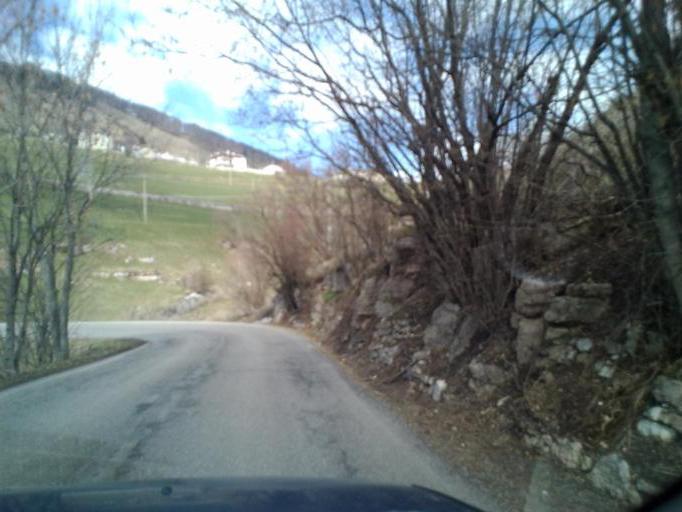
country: IT
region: Veneto
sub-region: Provincia di Verona
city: Erbezzo
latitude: 45.6488
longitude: 10.9955
